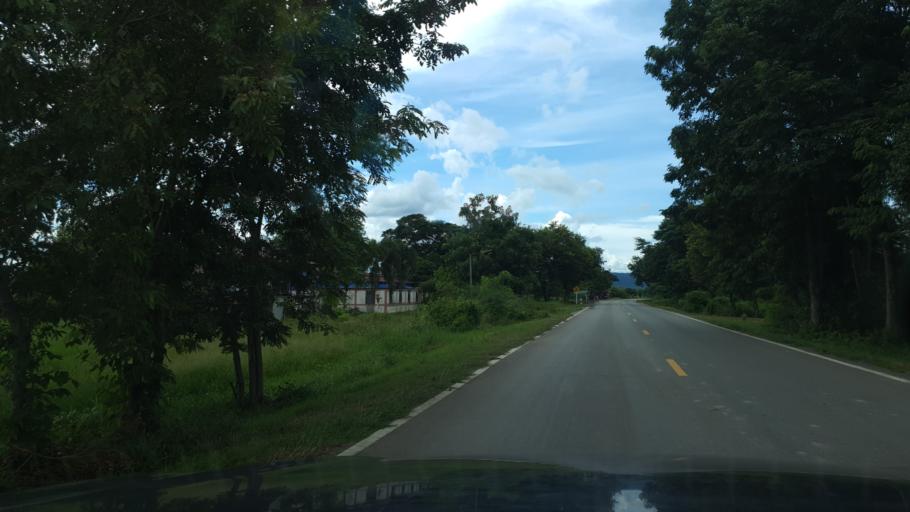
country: TH
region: Sukhothai
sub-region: Amphoe Si Satchanalai
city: Si Satchanalai
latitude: 17.4648
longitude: 99.7590
